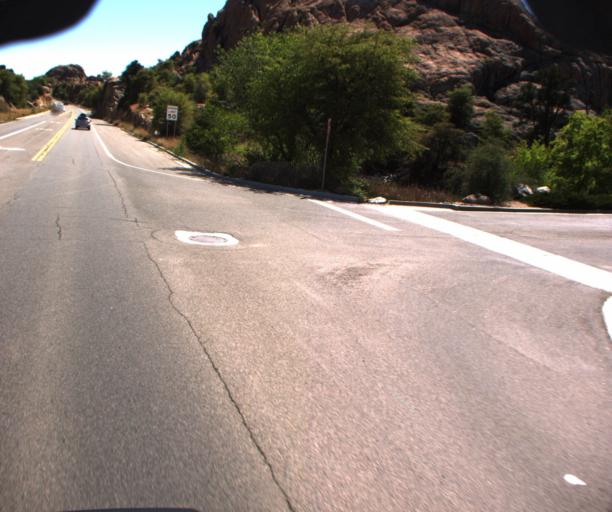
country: US
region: Arizona
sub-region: Yavapai County
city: Prescott
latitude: 34.6091
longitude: -112.4204
